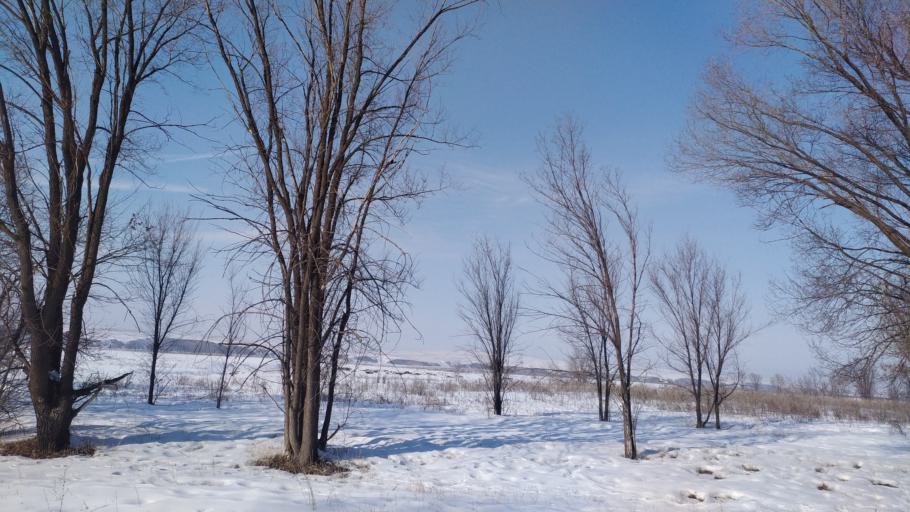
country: KZ
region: Almaty Oblysy
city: Burunday
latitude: 43.2375
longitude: 76.4154
